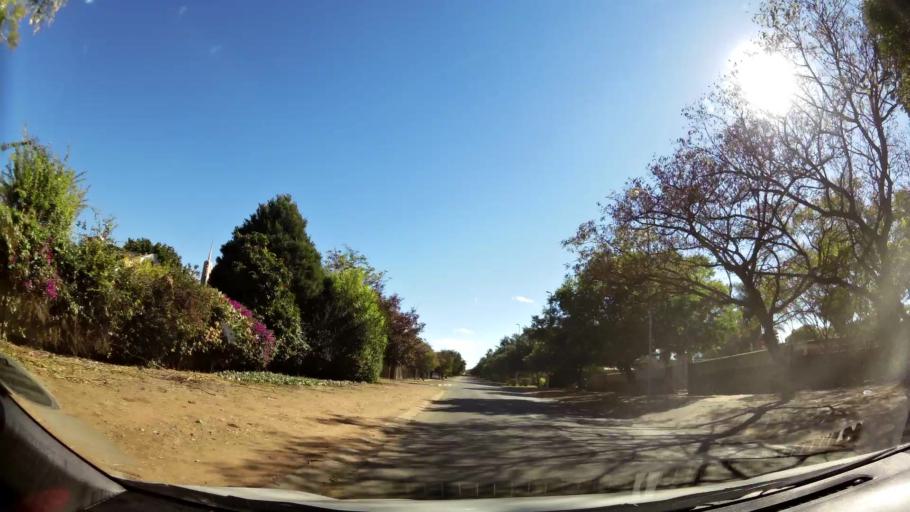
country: ZA
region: Limpopo
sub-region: Capricorn District Municipality
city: Polokwane
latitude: -23.9102
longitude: 29.4779
